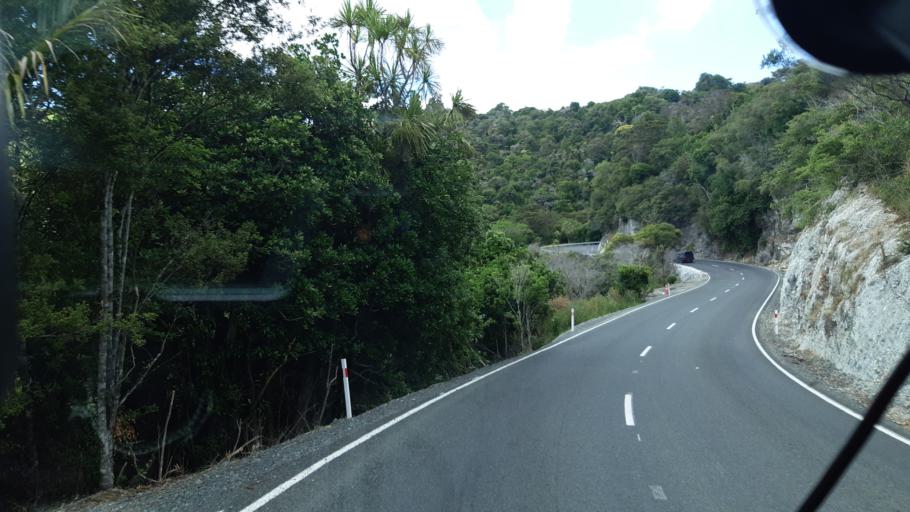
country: NZ
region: Northland
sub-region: Far North District
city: Taipa
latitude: -35.2445
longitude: 173.5354
